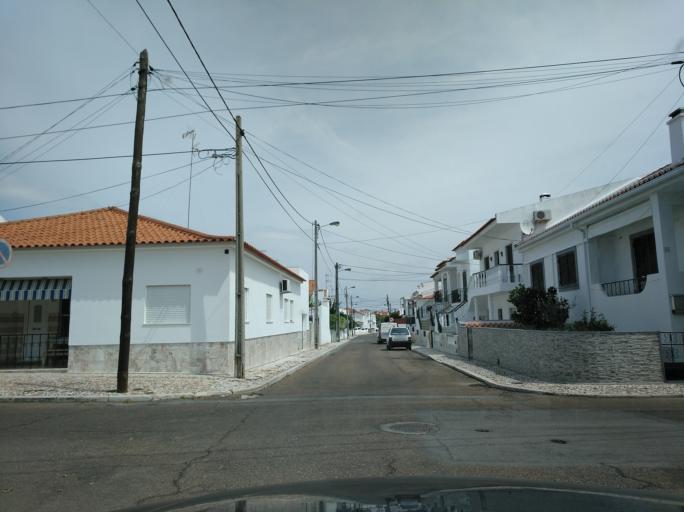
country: PT
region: Portalegre
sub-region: Campo Maior
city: Campo Maior
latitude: 39.0151
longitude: -7.0618
